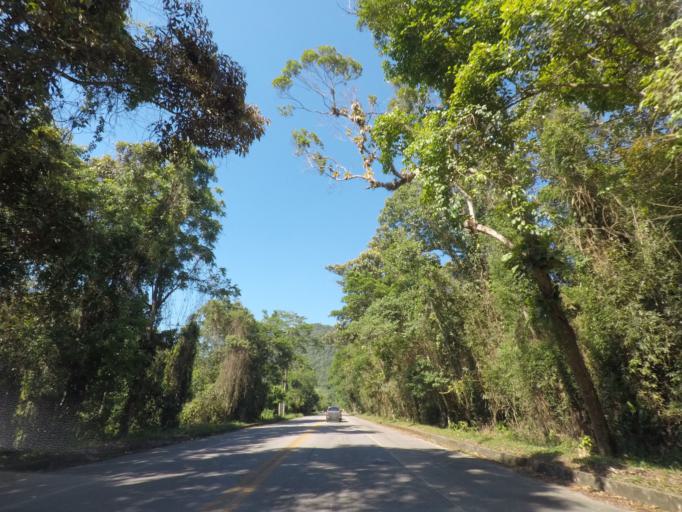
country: BR
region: Sao Paulo
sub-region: Ubatuba
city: Ubatuba
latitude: -23.3456
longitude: -44.9425
